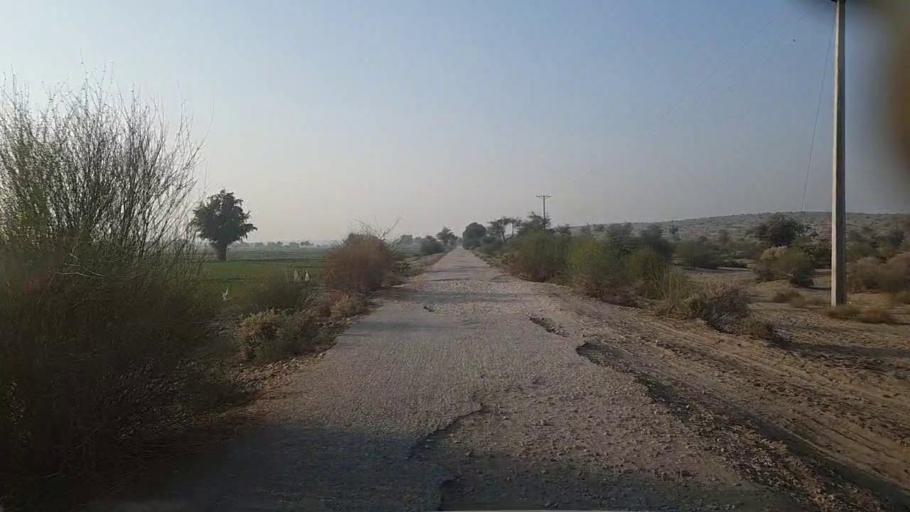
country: PK
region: Sindh
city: Pad Idan
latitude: 26.7165
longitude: 68.4625
